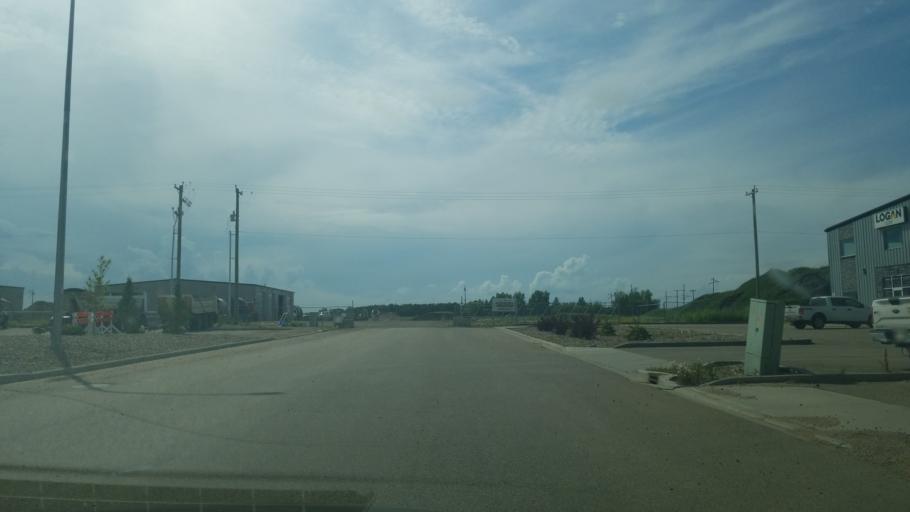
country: CA
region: Saskatchewan
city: Lloydminster
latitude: 53.2915
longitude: -110.0487
